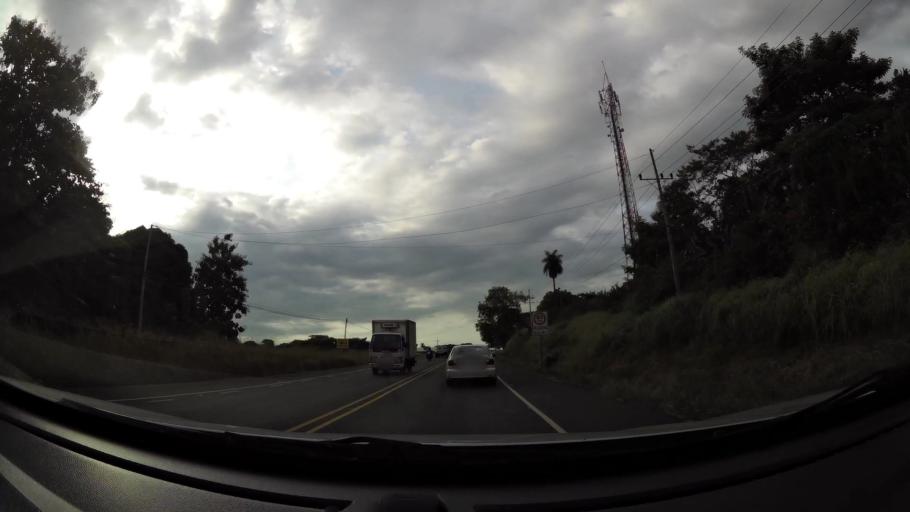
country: CR
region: Puntarenas
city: Esparza
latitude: 9.8932
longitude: -84.6502
